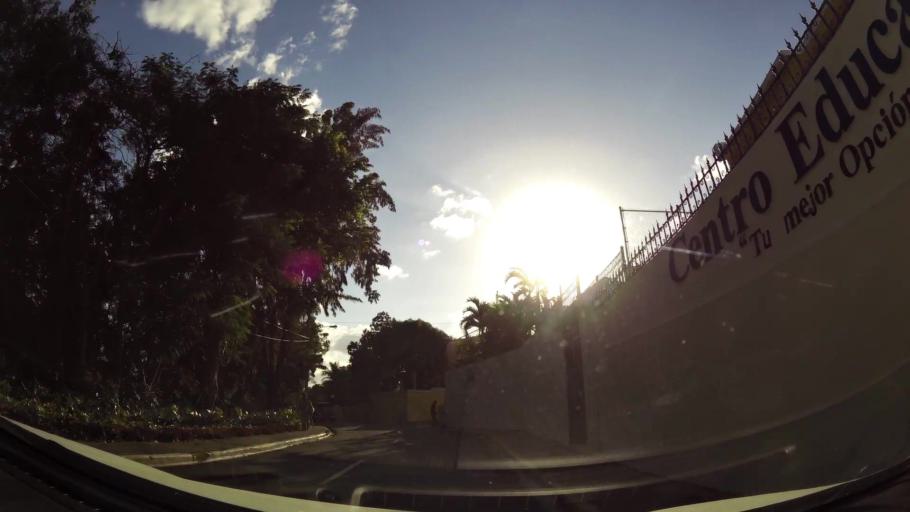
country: DO
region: Nacional
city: Santo Domingo
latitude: 18.4934
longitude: -69.9675
